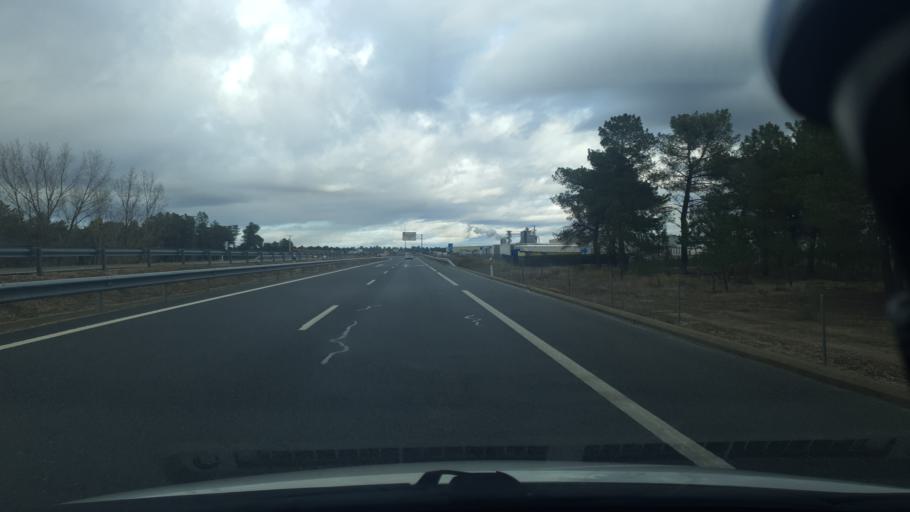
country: ES
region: Castille and Leon
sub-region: Provincia de Segovia
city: Sanchonuno
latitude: 41.3364
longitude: -4.3062
